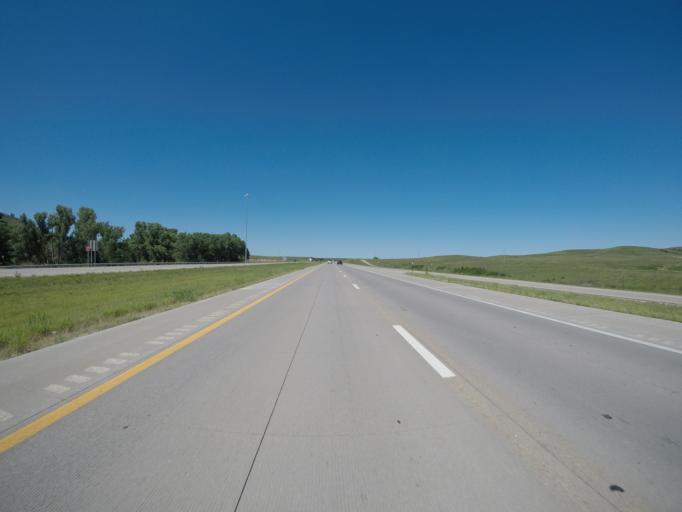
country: US
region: Kansas
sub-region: Ellsworth County
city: Ellsworth
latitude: 38.8584
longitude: -98.1123
